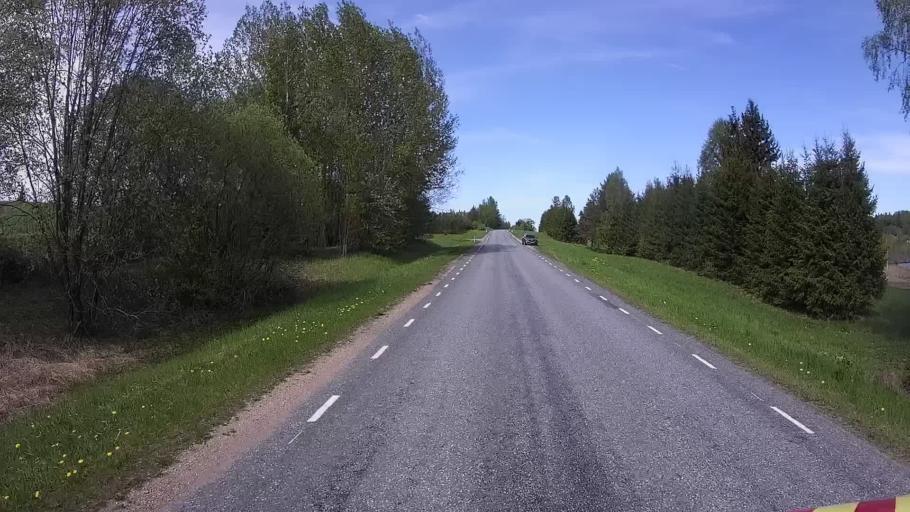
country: EE
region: Valgamaa
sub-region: Valga linn
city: Valga
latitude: 57.6823
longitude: 26.2795
